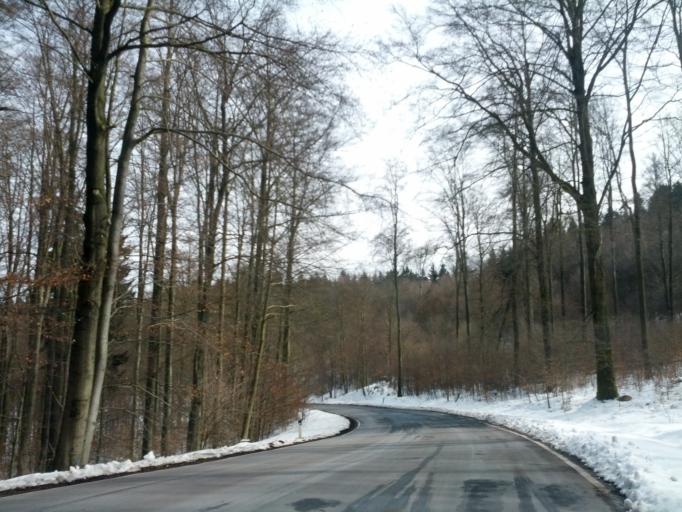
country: DE
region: Thuringia
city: Ruhla
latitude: 50.8717
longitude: 10.3752
